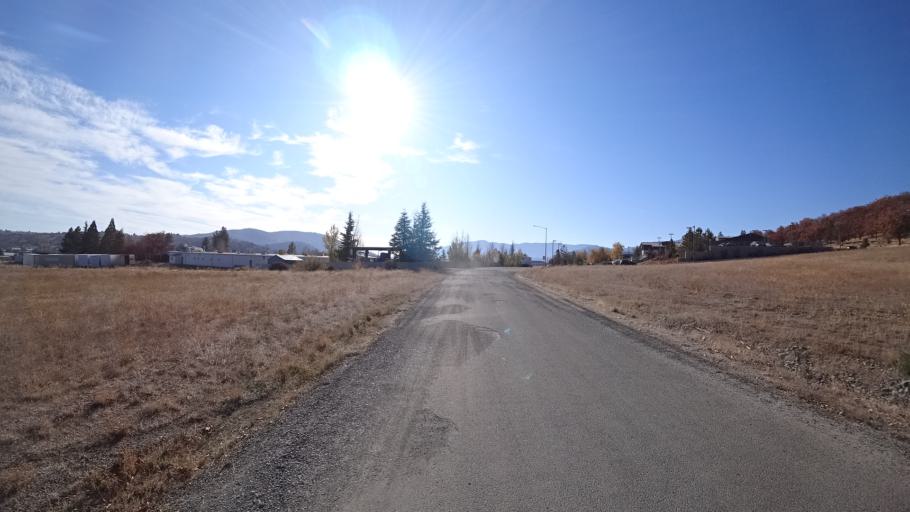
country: US
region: California
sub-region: Siskiyou County
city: Yreka
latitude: 41.7087
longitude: -122.6481
